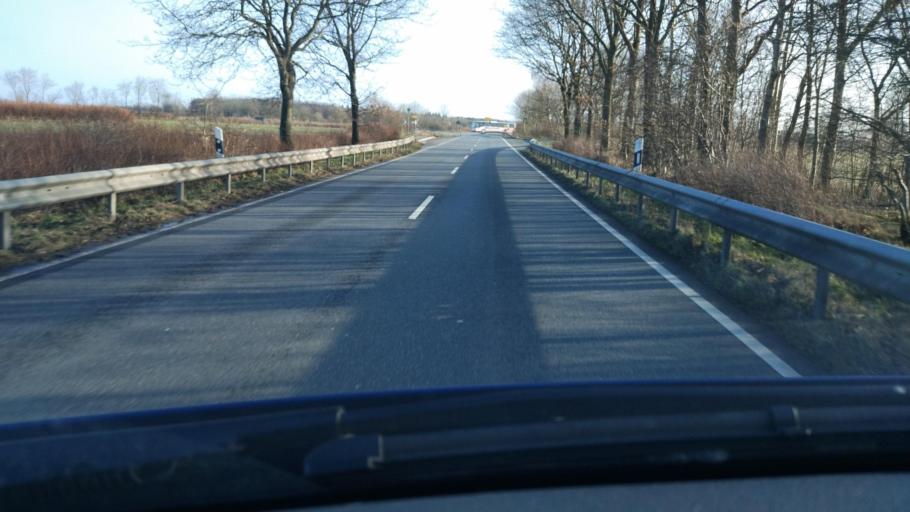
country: DE
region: Schleswig-Holstein
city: Jerrishoe
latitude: 54.6762
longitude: 9.3711
